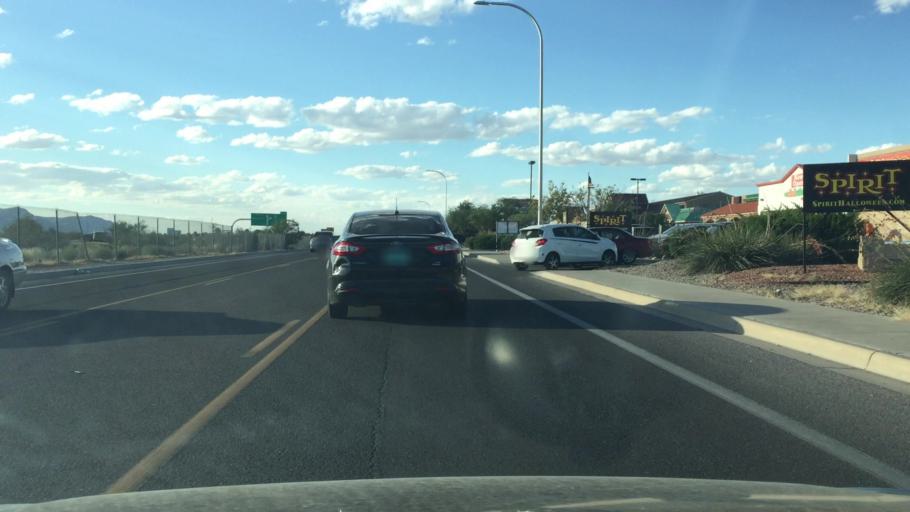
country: US
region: New Mexico
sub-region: Dona Ana County
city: Las Cruces
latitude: 32.3307
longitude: -106.7569
